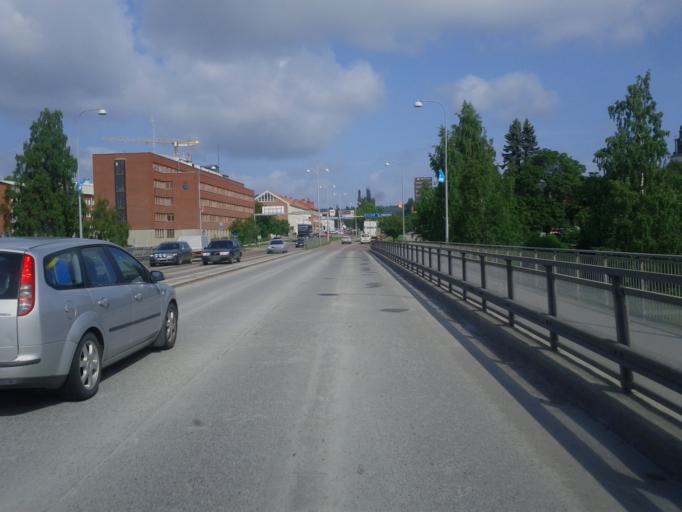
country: SE
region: Vaesterbotten
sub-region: Skelleftea Kommun
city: Skelleftea
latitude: 64.7474
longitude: 20.9600
